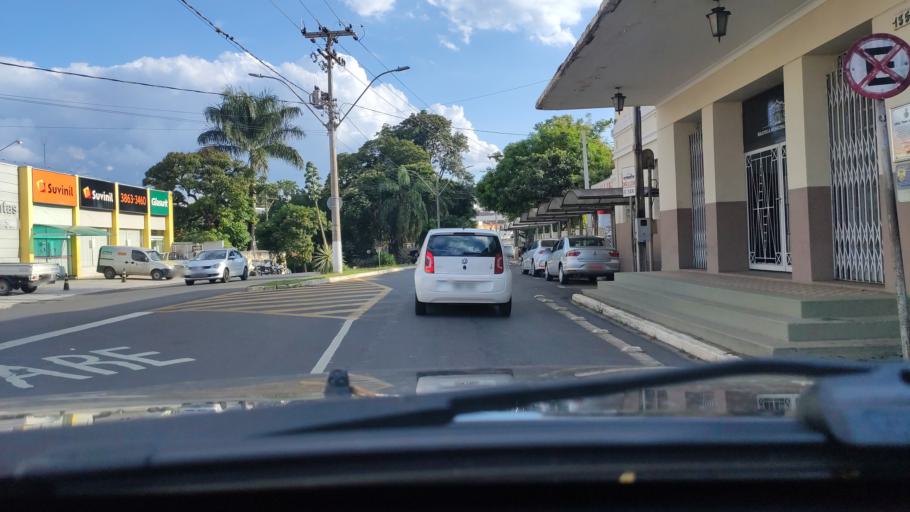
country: BR
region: Sao Paulo
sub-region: Itapira
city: Itapira
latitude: -22.4377
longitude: -46.8258
